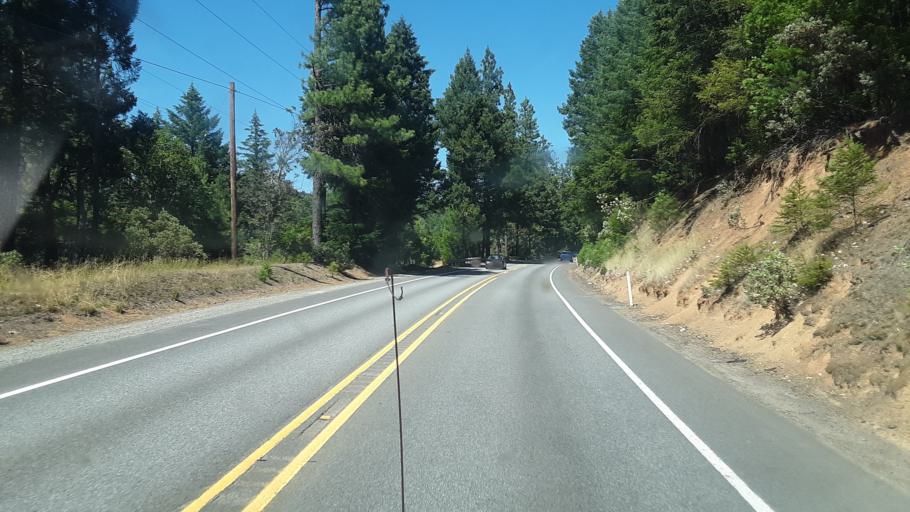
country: US
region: Oregon
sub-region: Josephine County
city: Cave Junction
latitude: 42.3147
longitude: -123.6053
